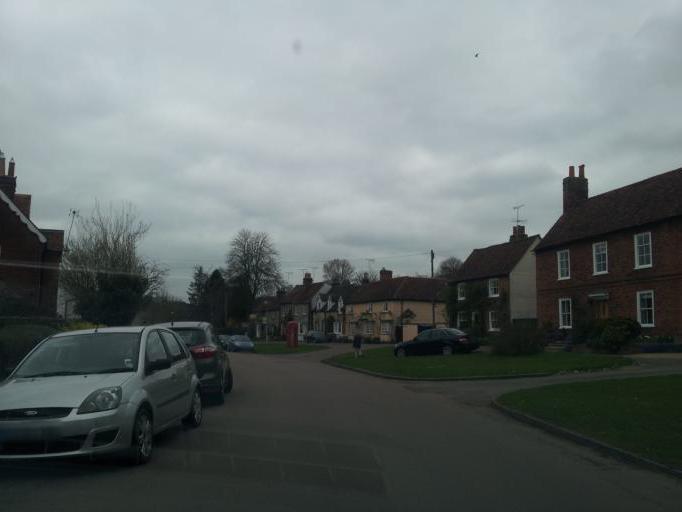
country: GB
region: England
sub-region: Hertfordshire
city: Much Hadham
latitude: 51.8818
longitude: 0.0272
